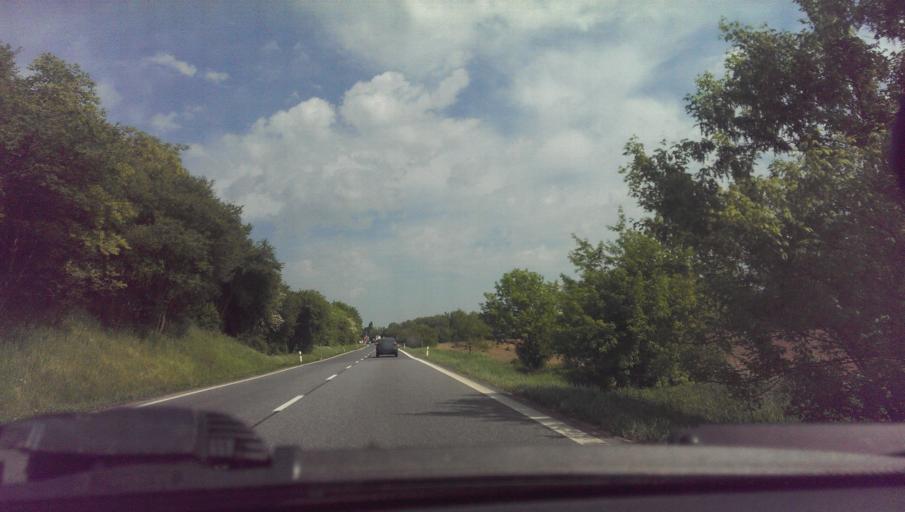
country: CZ
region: Zlin
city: Spytihnev
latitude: 49.1557
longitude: 17.5042
